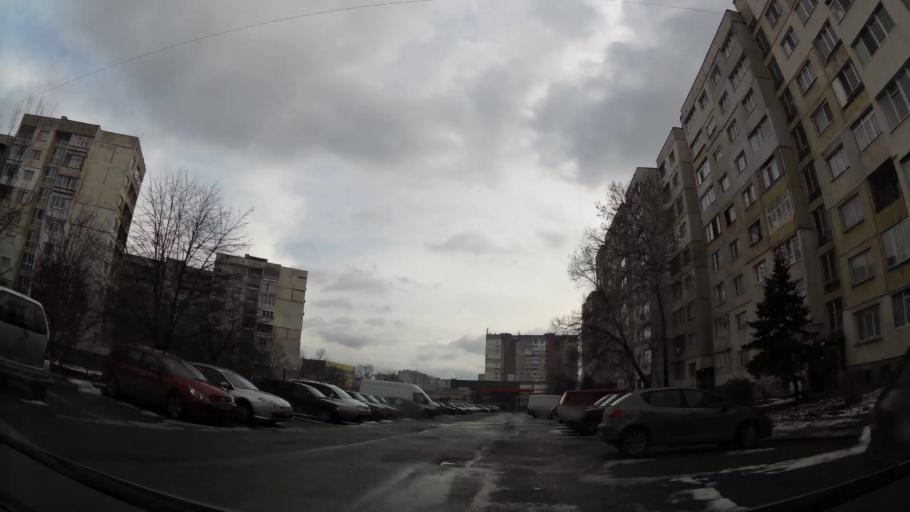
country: BG
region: Sofiya
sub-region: Obshtina Bozhurishte
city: Bozhurishte
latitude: 42.7139
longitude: 23.2384
